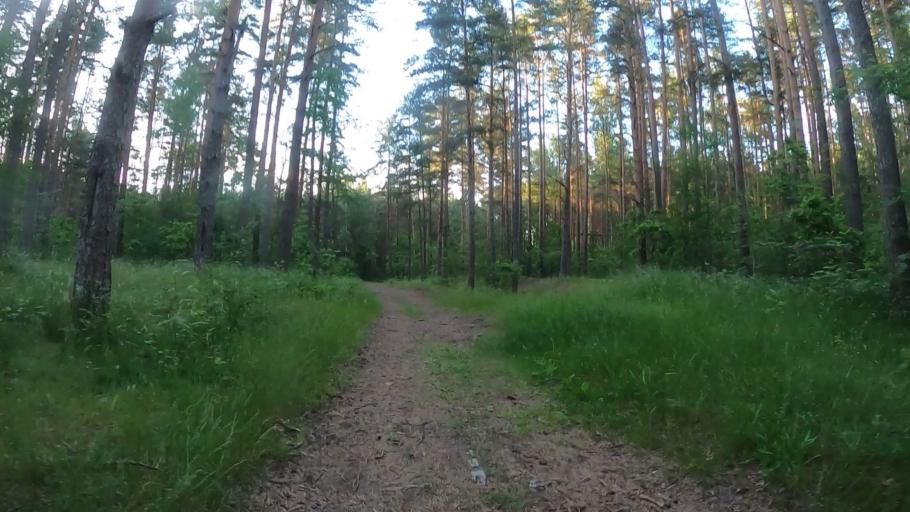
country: LV
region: Marupe
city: Marupe
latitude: 56.8855
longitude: 24.0314
